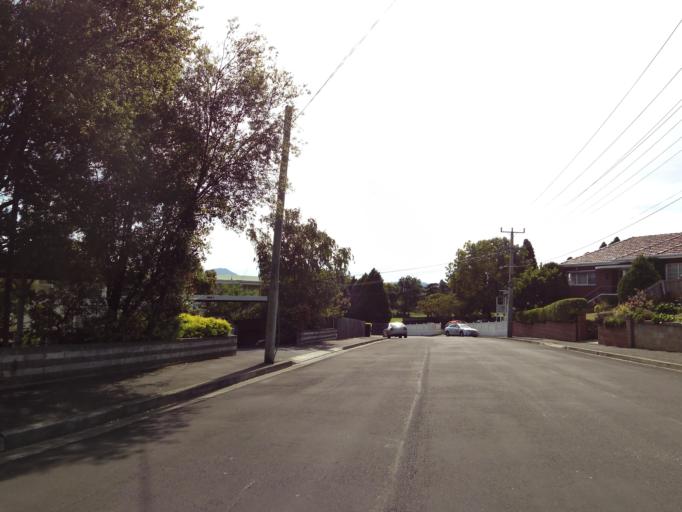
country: AU
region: Tasmania
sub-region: Hobart
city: New Town
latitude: -42.8525
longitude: 147.3109
